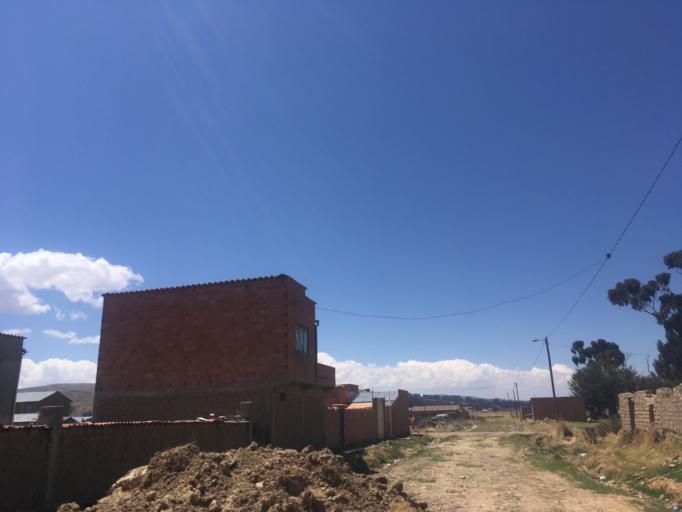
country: BO
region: La Paz
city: Huatajata
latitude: -16.1930
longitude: -68.7441
